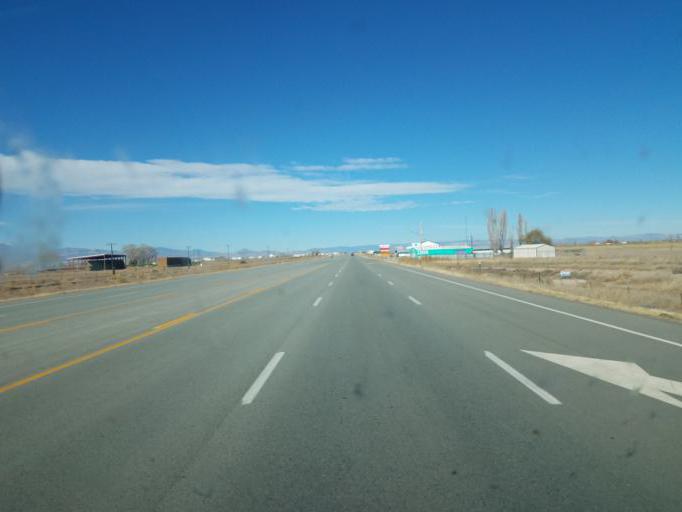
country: US
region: Colorado
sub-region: Rio Grande County
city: Monte Vista
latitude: 37.5302
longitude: -106.0242
